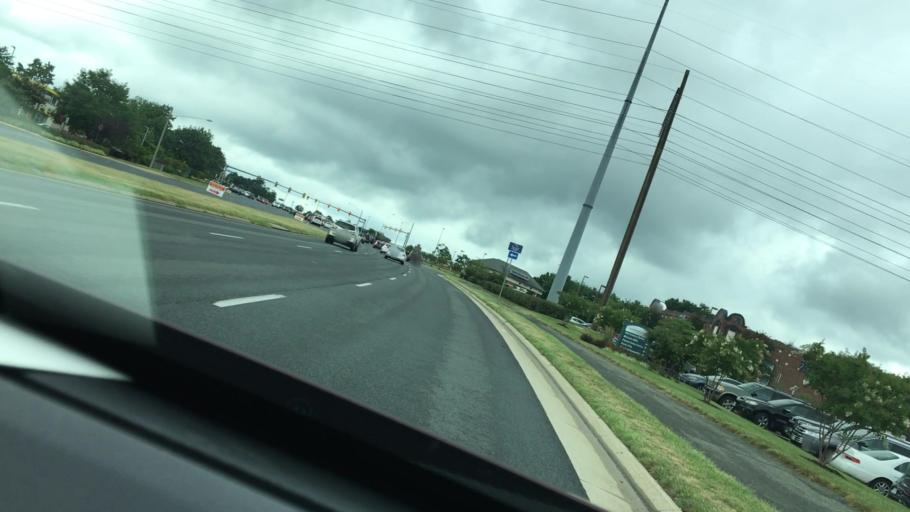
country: US
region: Virginia
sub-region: Prince William County
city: Potomac Mills
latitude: 38.6515
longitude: -77.2961
